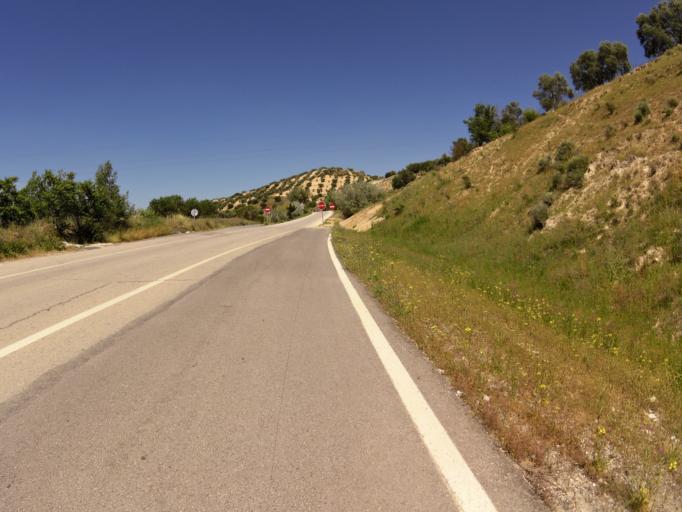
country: ES
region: Andalusia
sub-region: Provincia de Granada
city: Salar
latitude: 37.1704
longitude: -4.0860
